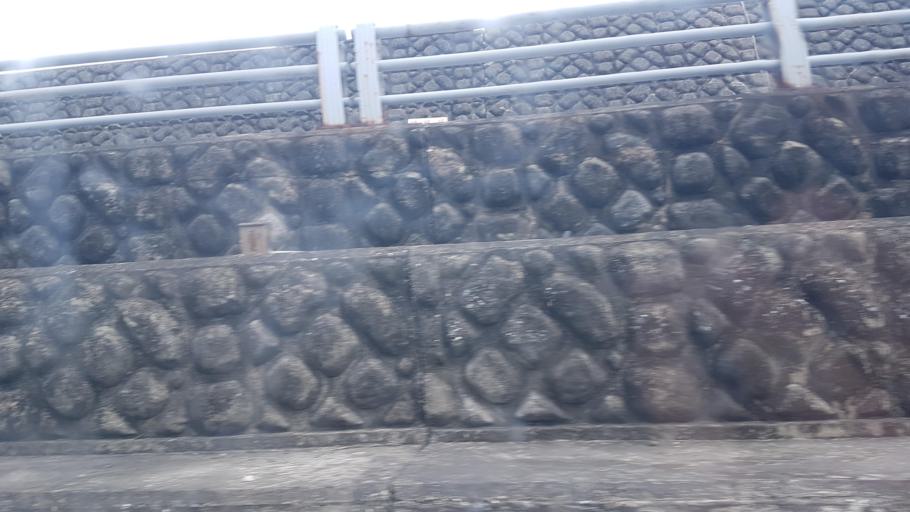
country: TW
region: Taiwan
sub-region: Hualien
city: Hualian
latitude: 23.9982
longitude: 121.6414
